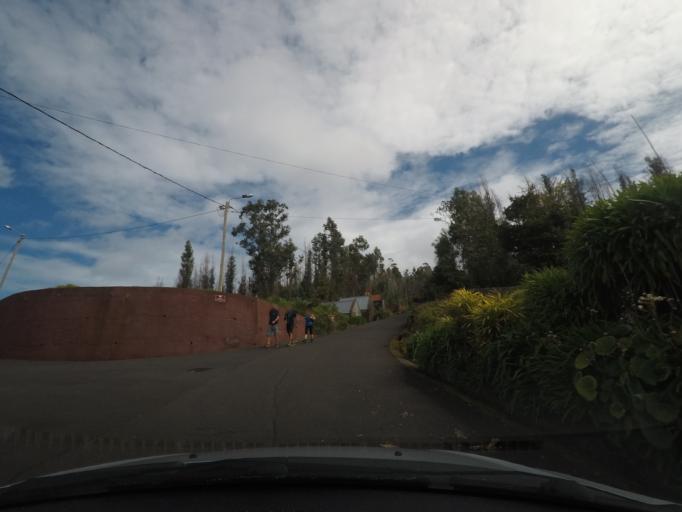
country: PT
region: Madeira
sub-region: Calheta
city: Faja da Ovelha
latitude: 32.8304
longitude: -17.2302
